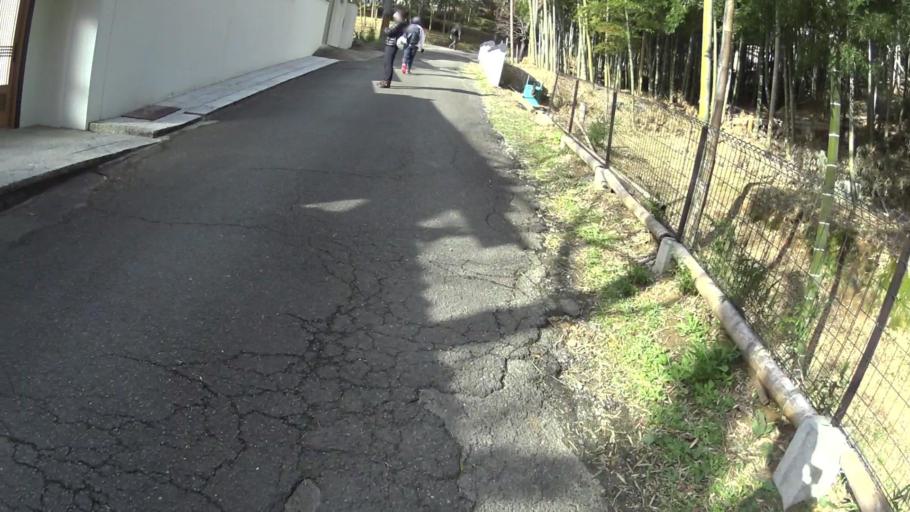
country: JP
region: Kyoto
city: Kyoto
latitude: 34.9633
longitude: 135.7862
